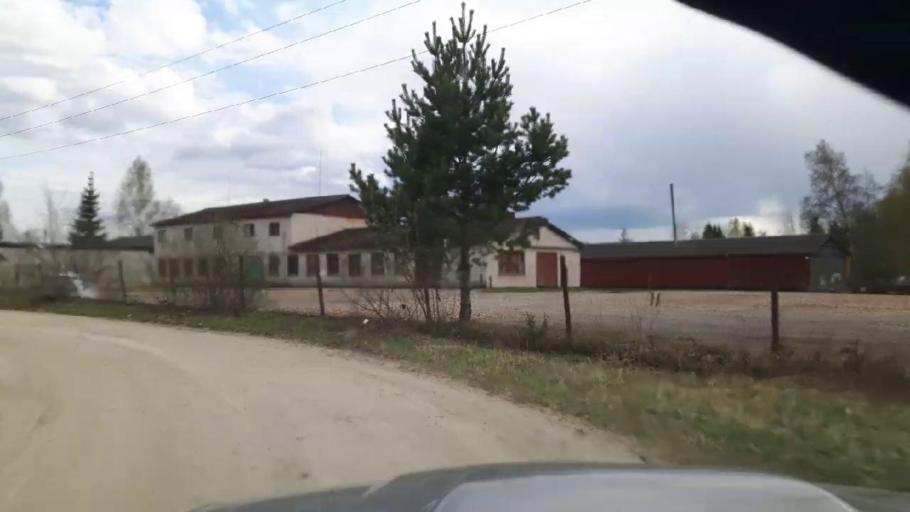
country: EE
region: Paernumaa
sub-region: Tootsi vald
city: Tootsi
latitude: 58.5199
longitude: 24.8167
